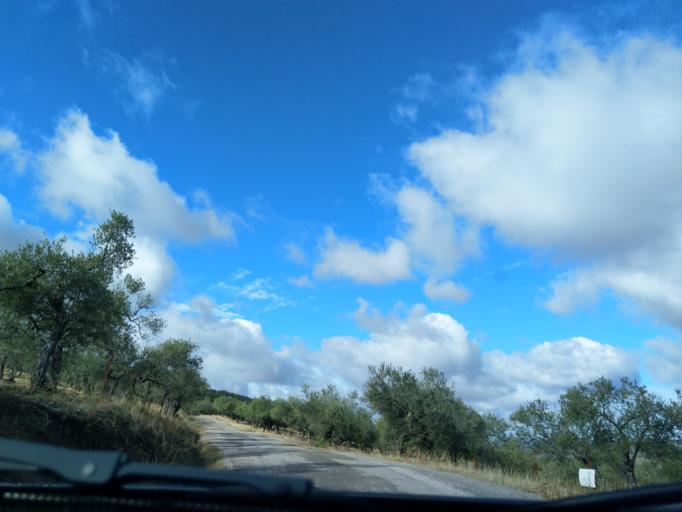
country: ES
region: Extremadura
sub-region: Provincia de Badajoz
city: Reina
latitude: 38.1293
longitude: -5.9276
